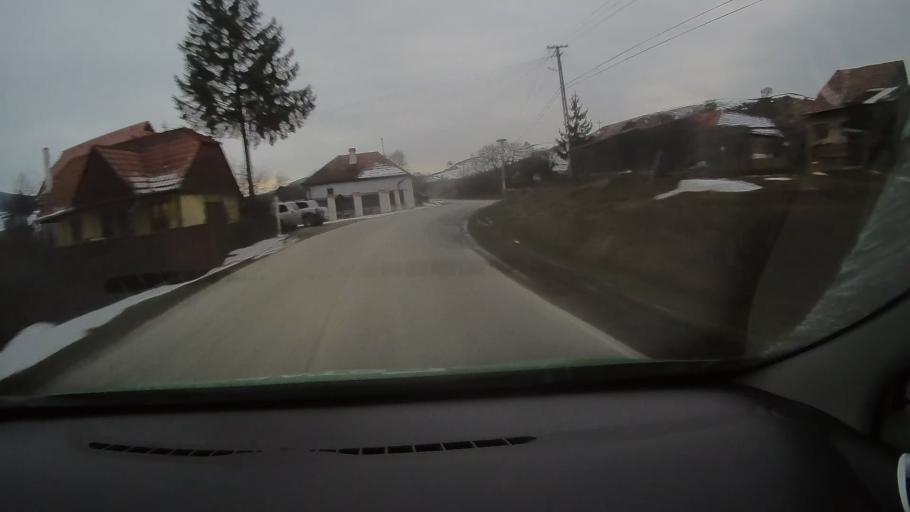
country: RO
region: Harghita
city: Taureni
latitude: 46.2395
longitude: 25.2529
